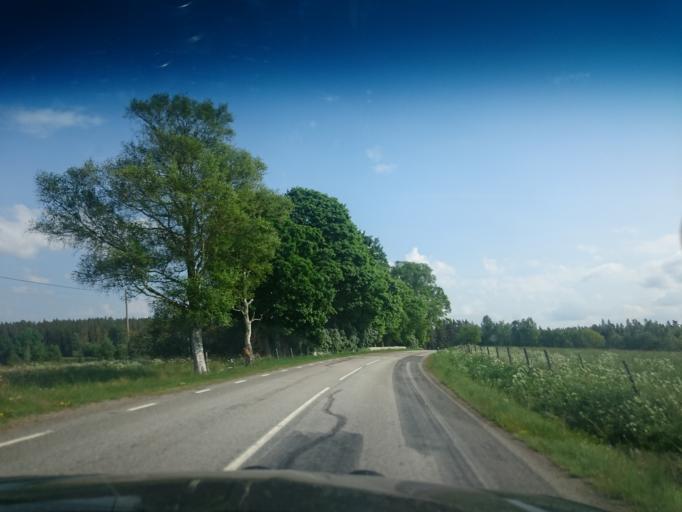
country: SE
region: Joenkoeping
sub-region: Vetlanda Kommun
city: Vetlanda
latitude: 57.3806
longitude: 15.0174
